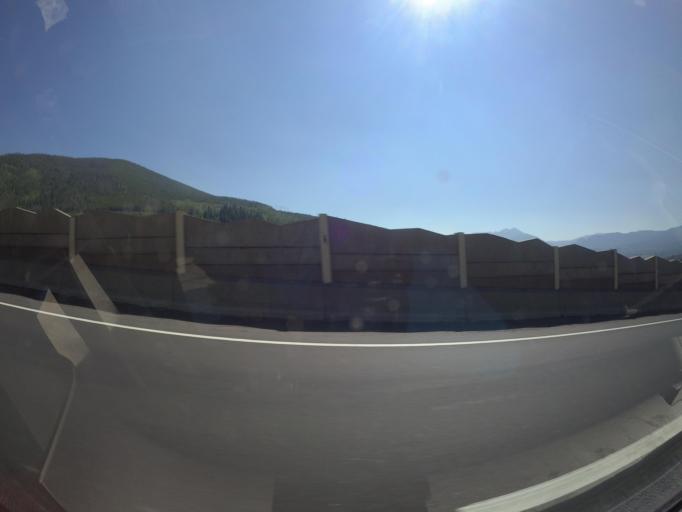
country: US
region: Colorado
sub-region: Summit County
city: Silverthorne
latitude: 39.6459
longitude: -106.0343
